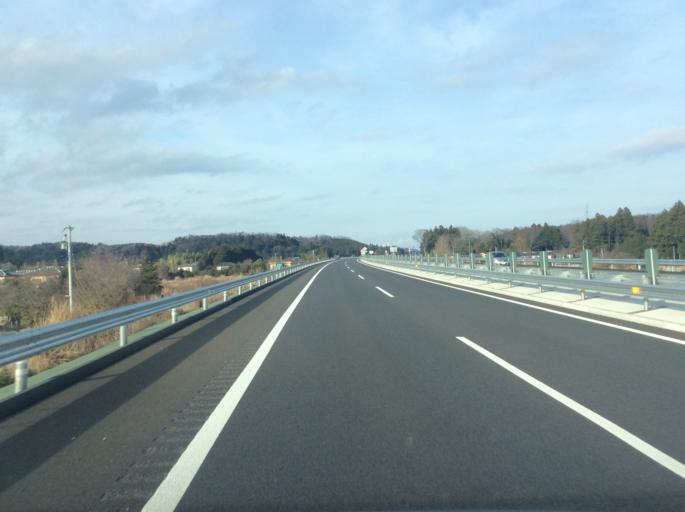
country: JP
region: Fukushima
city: Namie
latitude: 37.4053
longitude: 140.9628
